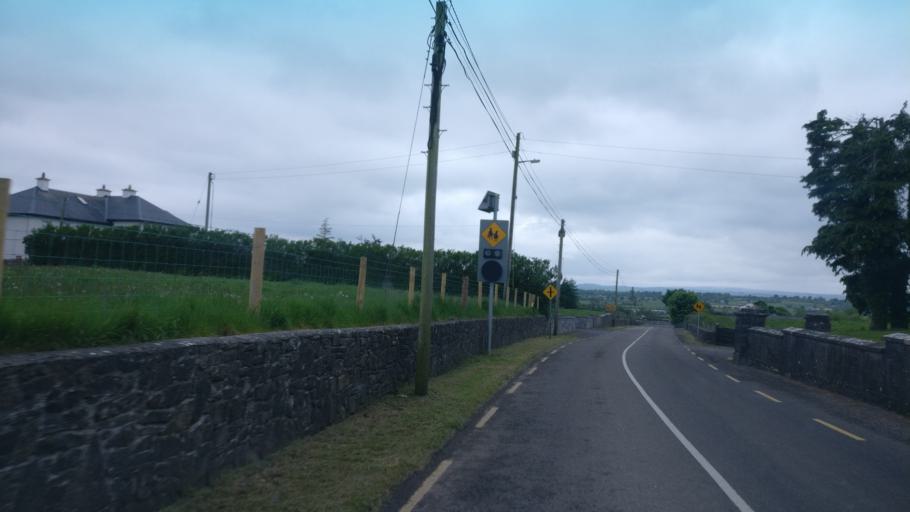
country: IE
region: Connaught
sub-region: County Galway
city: Portumna
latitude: 53.1126
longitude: -8.2838
